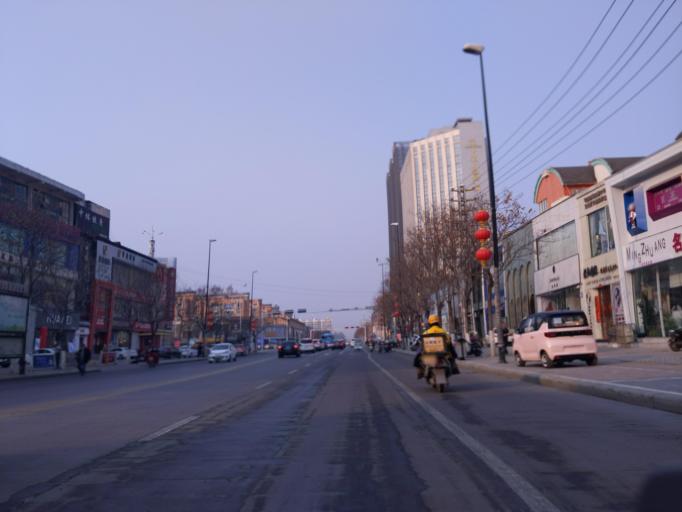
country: CN
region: Henan Sheng
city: Zhongyuanlu
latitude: 35.7693
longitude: 115.0584
